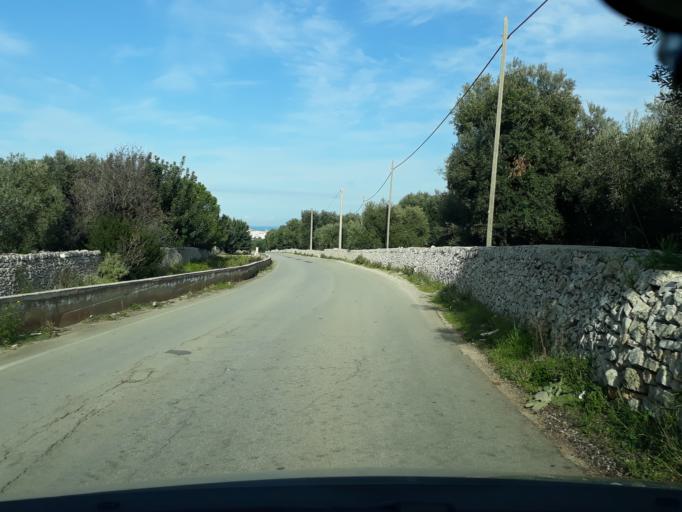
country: IT
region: Apulia
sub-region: Provincia di Brindisi
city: Fasano
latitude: 40.8183
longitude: 17.3574
